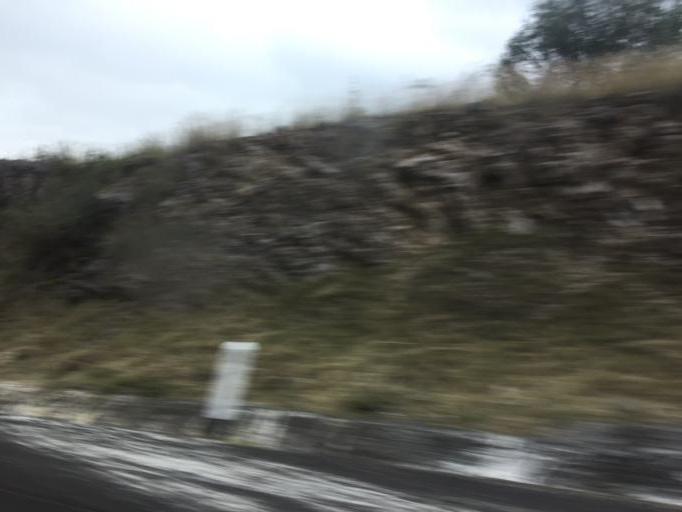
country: MX
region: Jalisco
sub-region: Zapotlan del Rey
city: Zapotlan del Rey
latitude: 20.4720
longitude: -102.9195
